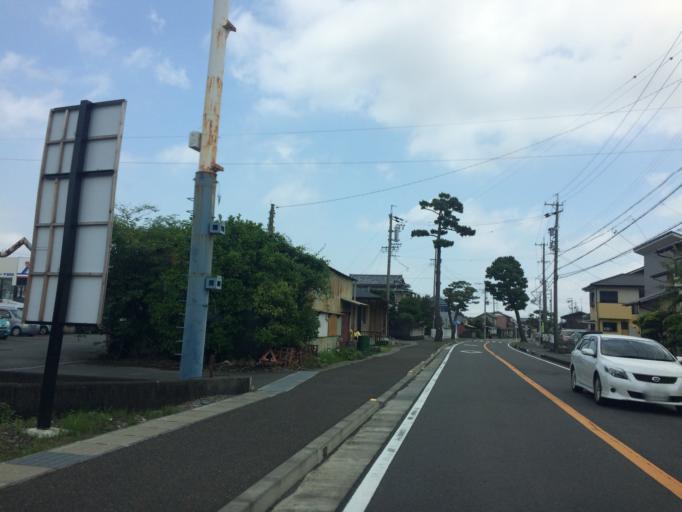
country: JP
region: Shizuoka
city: Shimada
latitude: 34.8426
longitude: 138.2218
